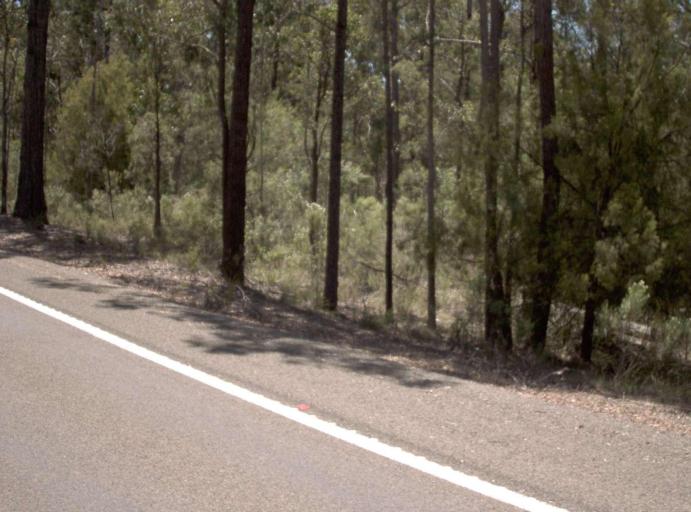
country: AU
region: Victoria
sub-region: East Gippsland
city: Lakes Entrance
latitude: -37.7673
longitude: 148.0589
